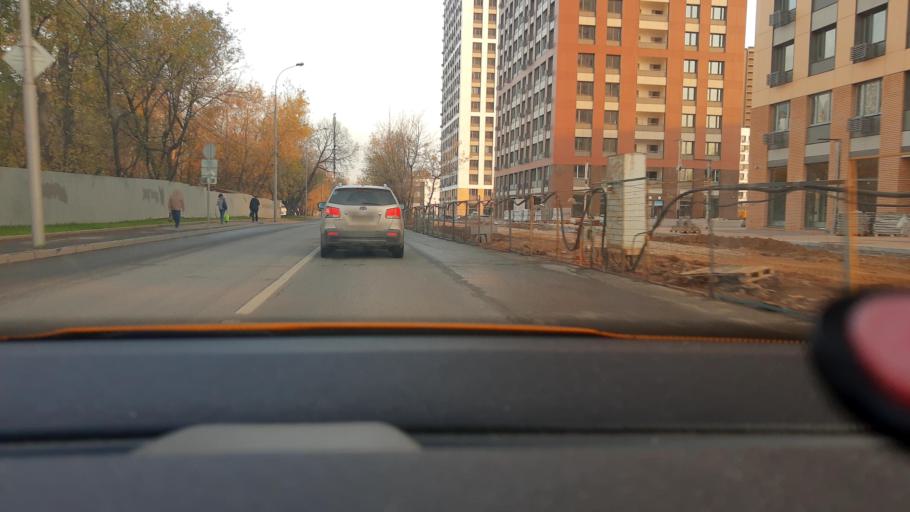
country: RU
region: Moskovskaya
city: Bogorodskoye
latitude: 55.8191
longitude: 37.7519
